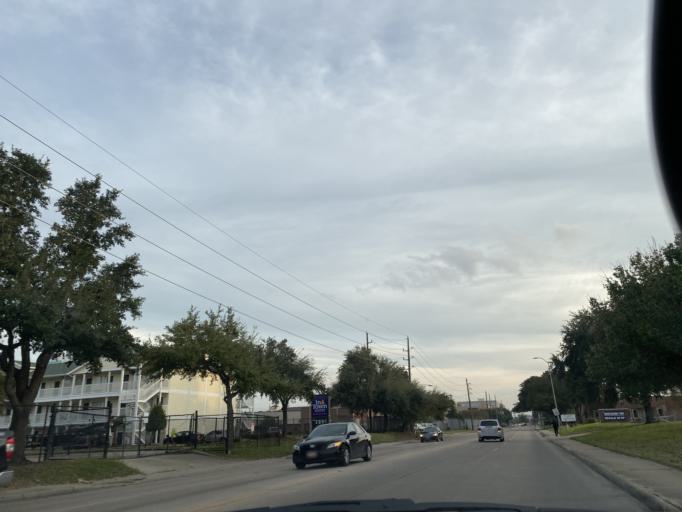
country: US
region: Texas
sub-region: Harris County
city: Bunker Hill Village
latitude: 29.7312
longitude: -95.5598
